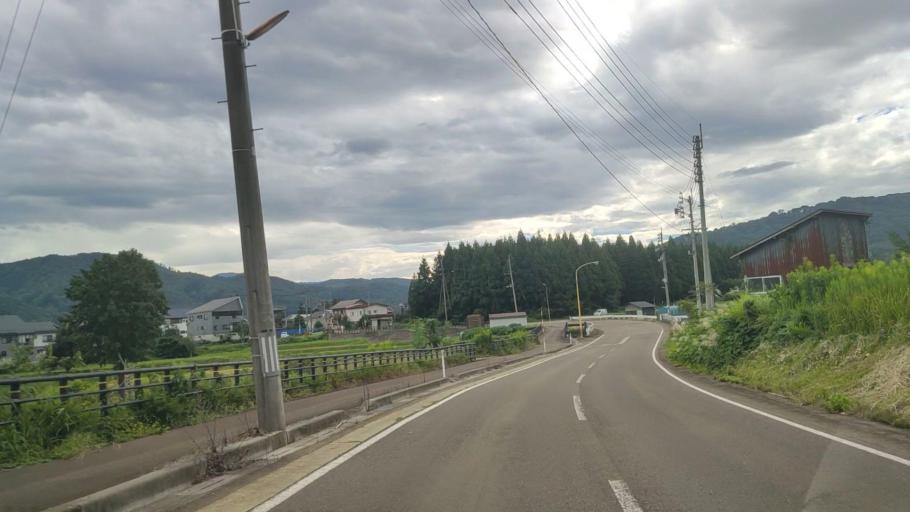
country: JP
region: Niigata
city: Arai
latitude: 37.0113
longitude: 138.2564
